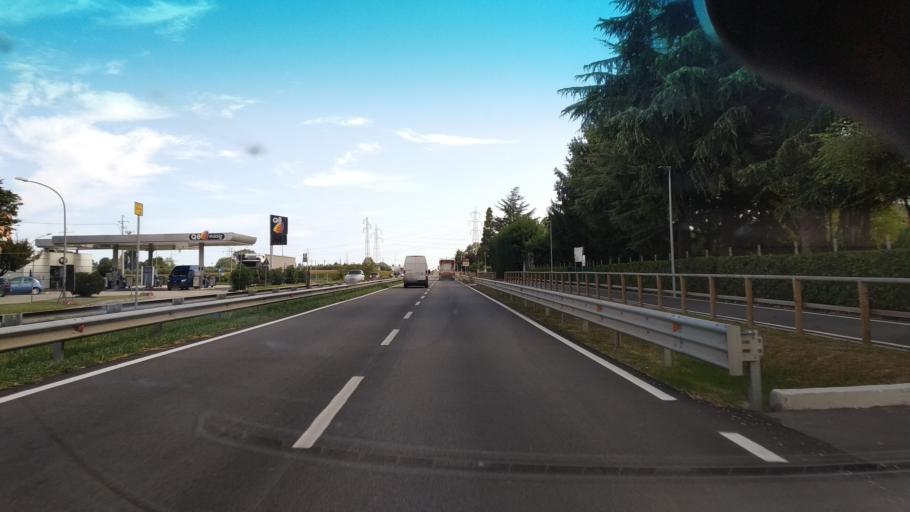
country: IT
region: Veneto
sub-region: Provincia di Padova
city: Villatora
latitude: 45.3827
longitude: 11.9684
